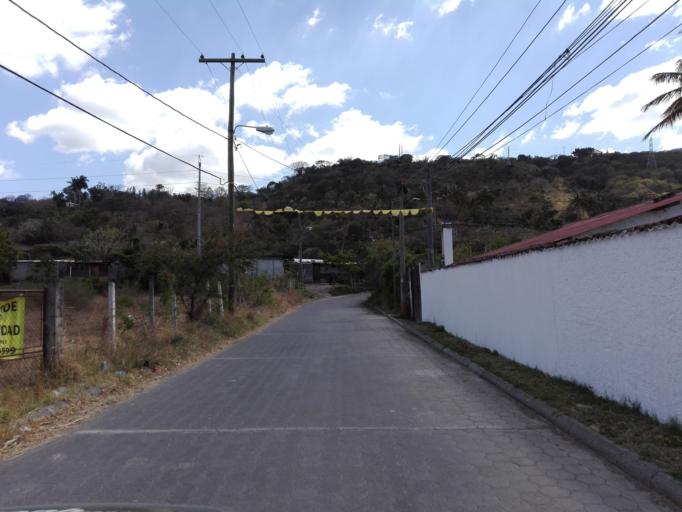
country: GT
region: Guatemala
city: Amatitlan
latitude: 14.4751
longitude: -90.6010
